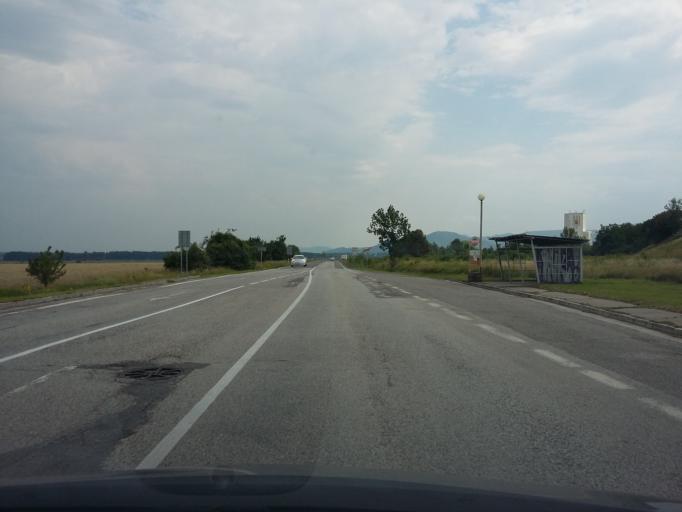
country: SK
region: Bratislavsky
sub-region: Okres Malacky
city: Malacky
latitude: 48.4585
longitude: 17.1779
